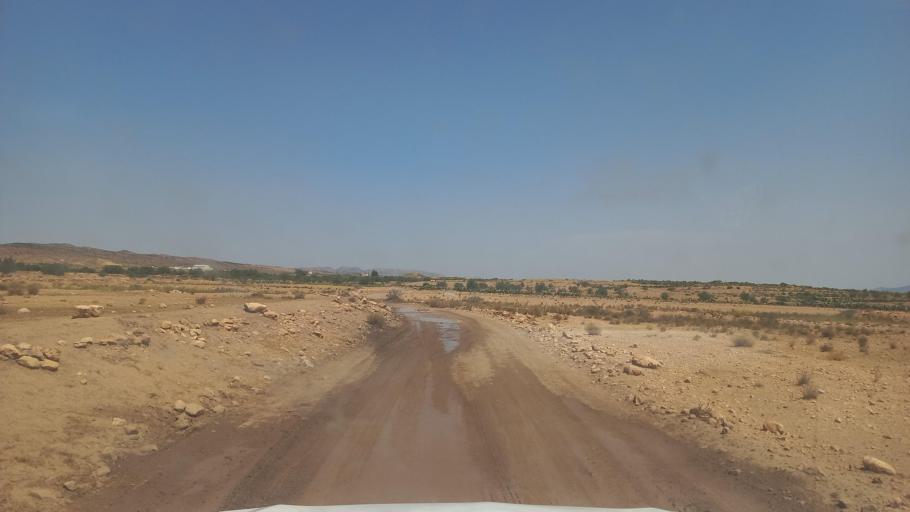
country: TN
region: Al Qasrayn
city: Kasserine
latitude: 35.2906
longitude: 8.9527
